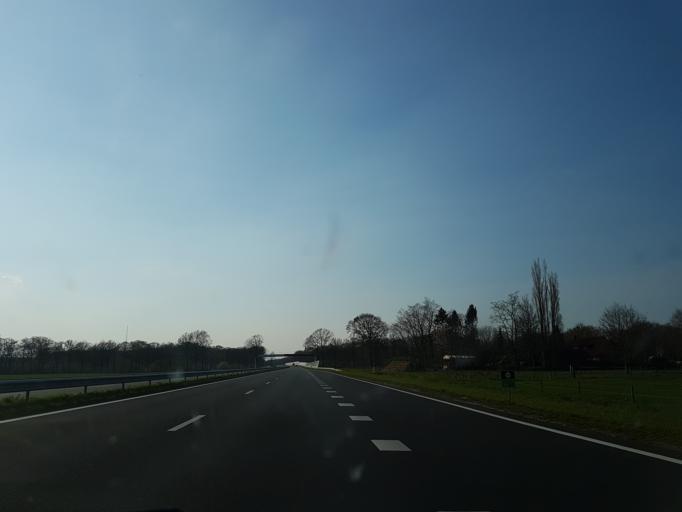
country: NL
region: Overijssel
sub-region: Gemeente Raalte
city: Heino
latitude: 52.4851
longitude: 6.1728
